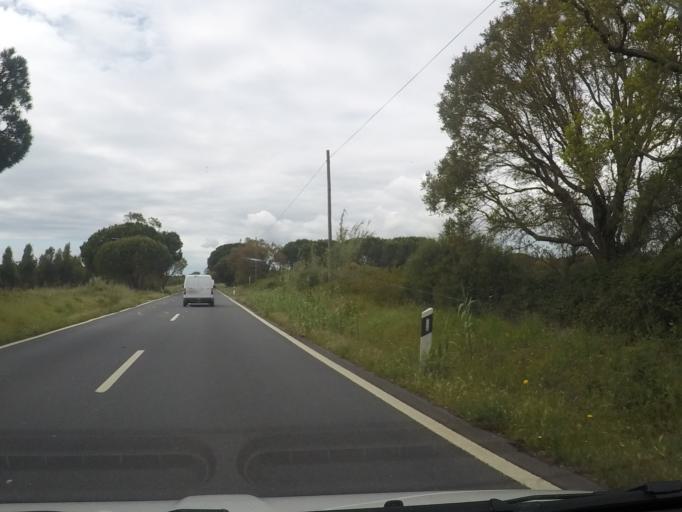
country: PT
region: Setubal
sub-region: Sines
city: Porto Covo
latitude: 37.8833
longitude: -8.7498
